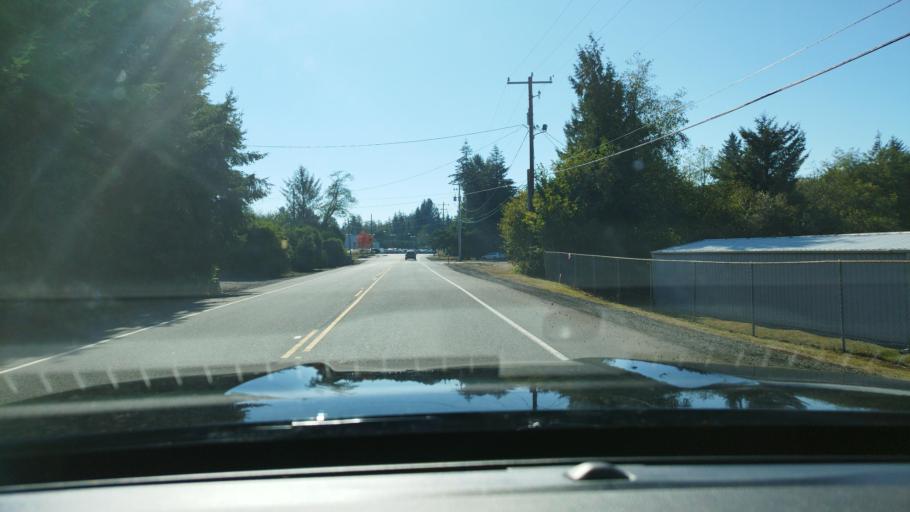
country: US
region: Oregon
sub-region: Clatsop County
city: Warrenton
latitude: 46.1511
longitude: -123.9183
